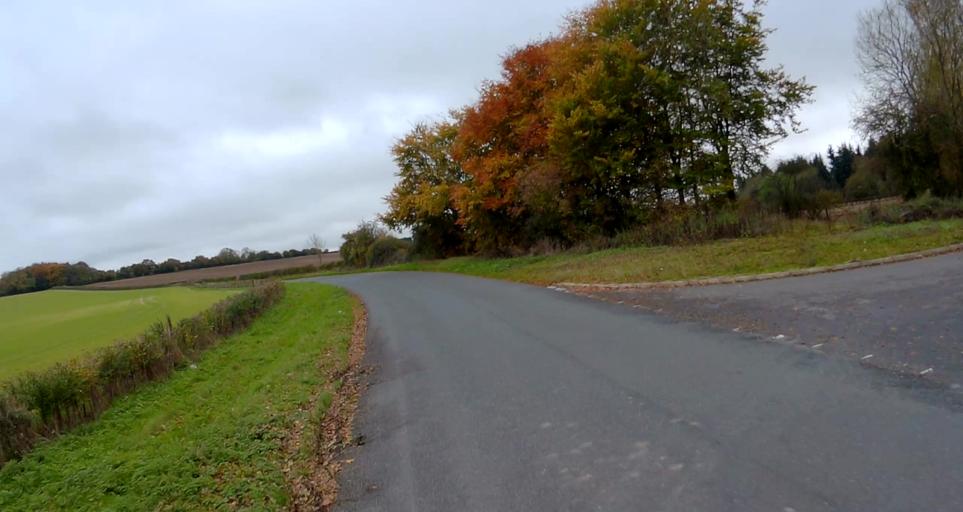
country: GB
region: England
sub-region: Hampshire
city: Basingstoke
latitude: 51.2267
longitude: -1.1270
